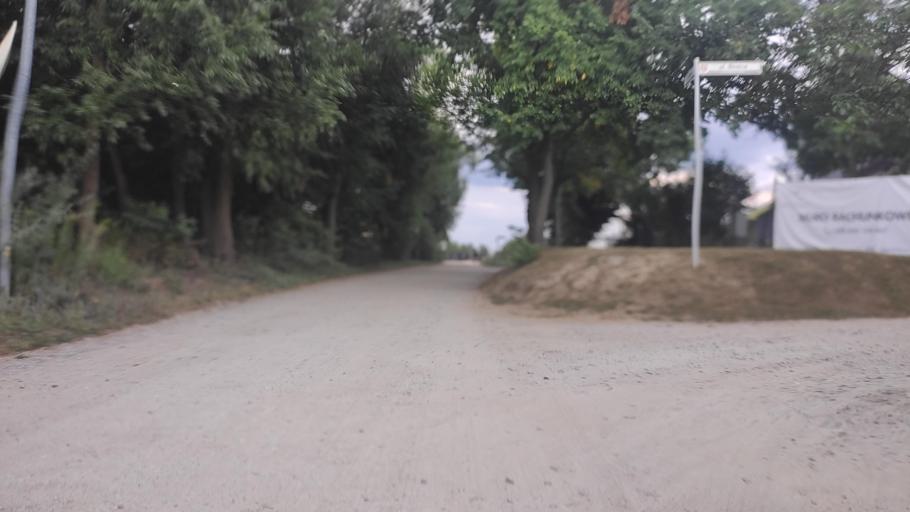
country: PL
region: Greater Poland Voivodeship
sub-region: Powiat poznanski
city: Swarzedz
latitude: 52.4247
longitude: 17.1115
